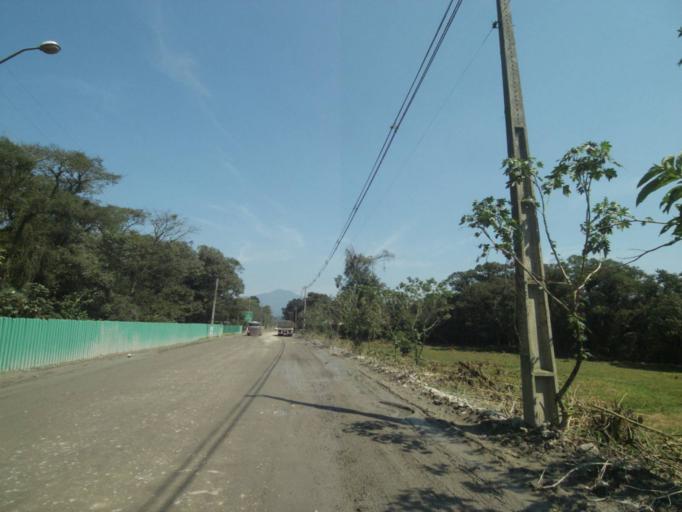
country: BR
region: Parana
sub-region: Paranagua
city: Paranagua
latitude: -25.5471
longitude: -48.5747
